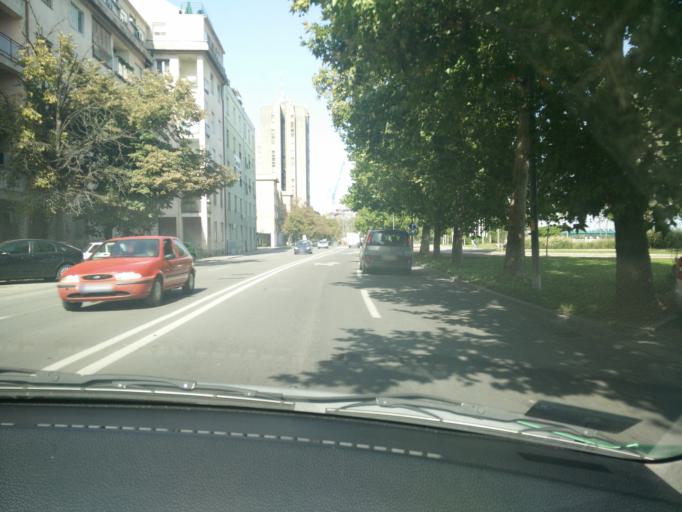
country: RS
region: Autonomna Pokrajina Vojvodina
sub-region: Juznobacki Okrug
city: Novi Sad
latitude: 45.2584
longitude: 19.8549
